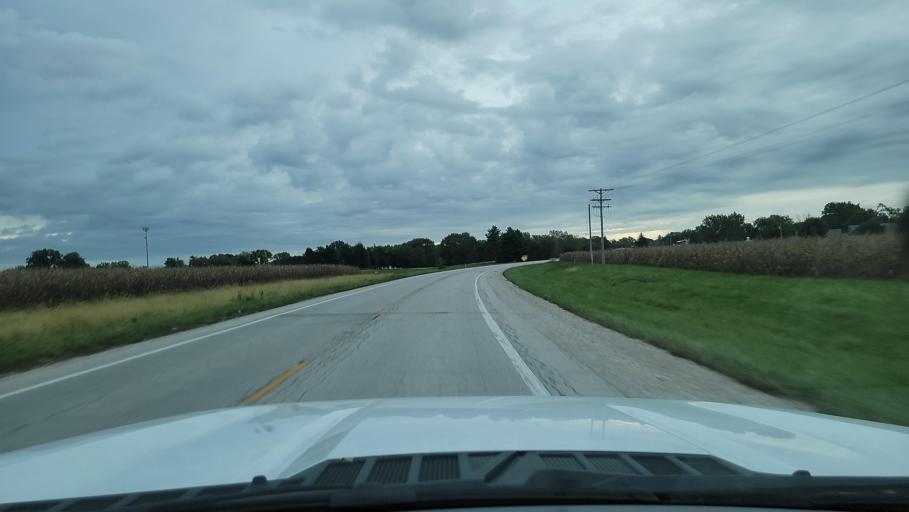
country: US
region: Illinois
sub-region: Schuyler County
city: Rushville
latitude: 40.1160
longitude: -90.5839
